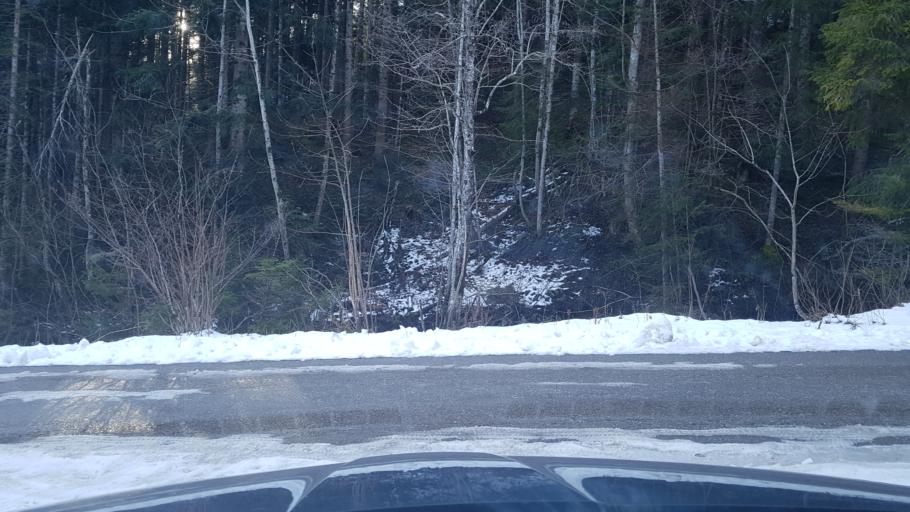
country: AT
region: Salzburg
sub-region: Politischer Bezirk Salzburg-Umgebung
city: Strobl
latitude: 47.5981
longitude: 13.4646
